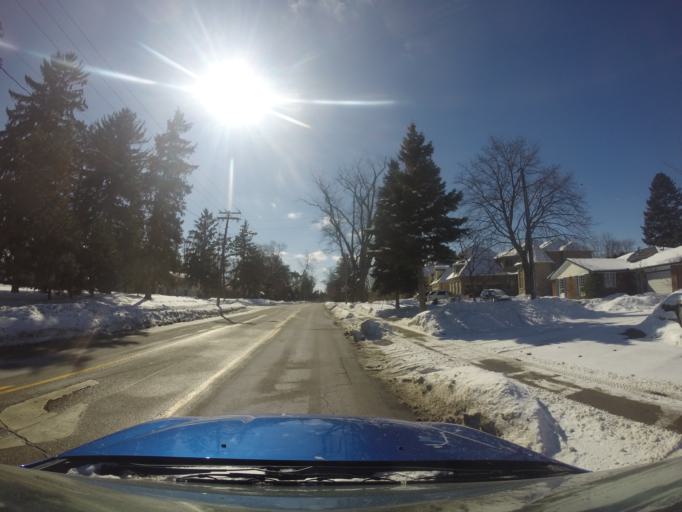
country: CA
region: Ontario
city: Burlington
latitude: 43.3422
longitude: -79.7660
